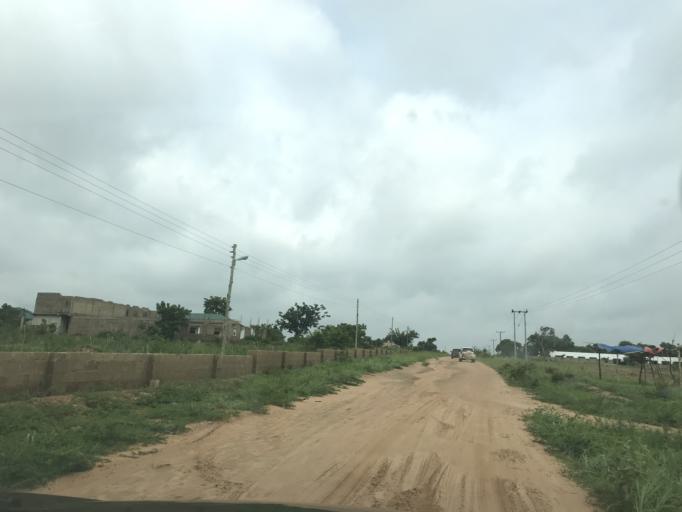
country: GH
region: Upper West
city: Wa
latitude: 10.0281
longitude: -2.4853
